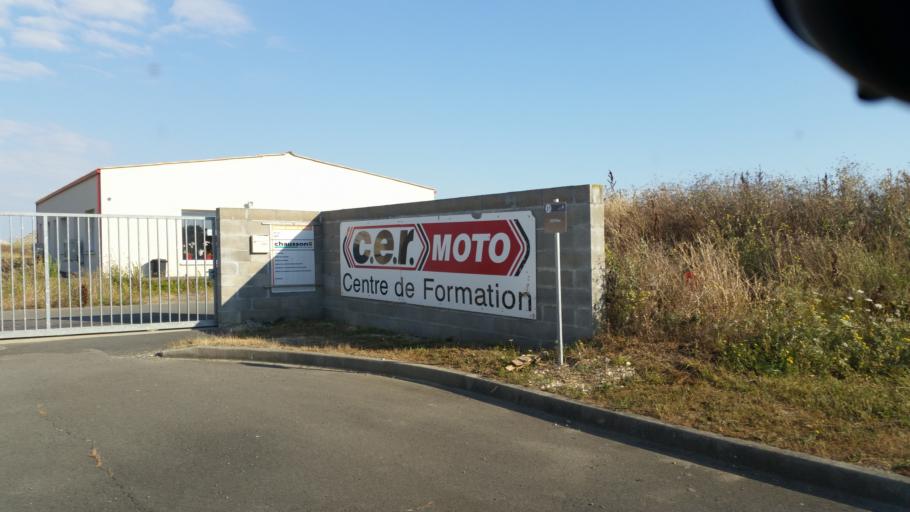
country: FR
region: Poitou-Charentes
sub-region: Departement de la Charente-Maritime
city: Saint-Jean-de-Liversay
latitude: 46.2332
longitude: -0.8842
